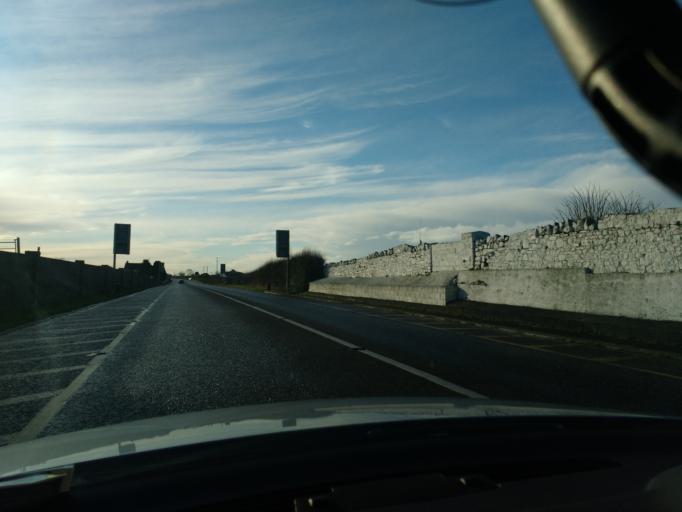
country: IE
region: Munster
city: Thurles
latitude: 52.6365
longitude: -7.7434
